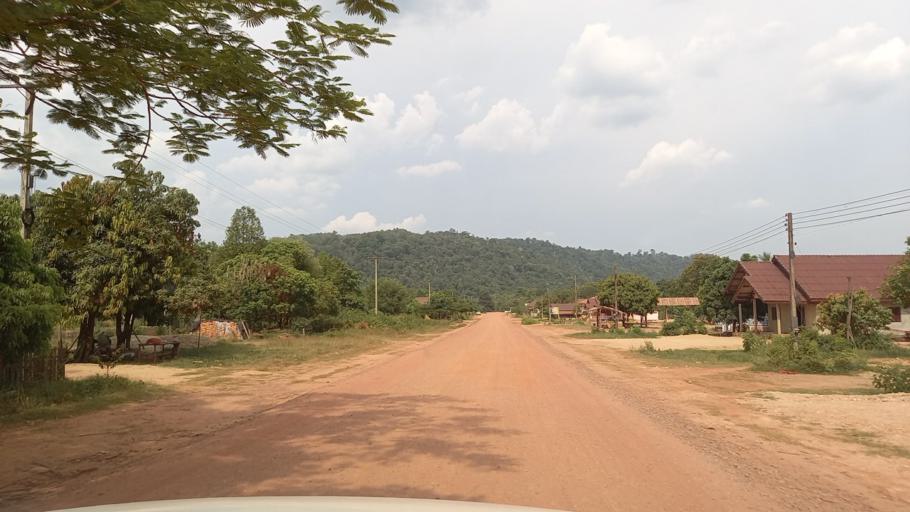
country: LA
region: Bolikhamxai
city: Bolikhan
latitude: 18.5571
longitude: 103.7366
